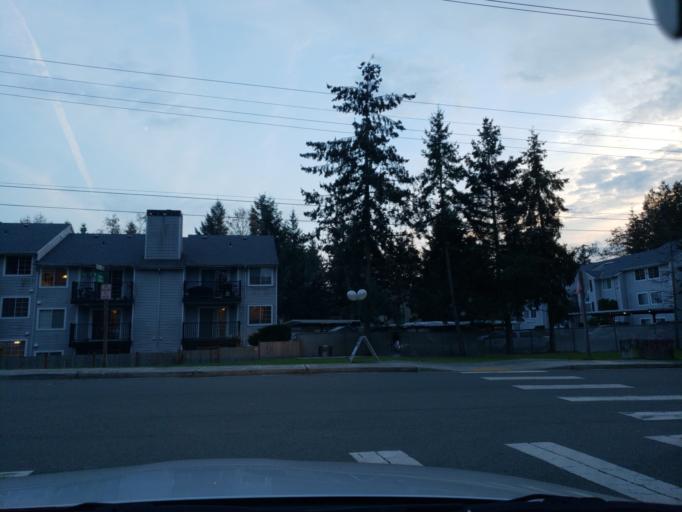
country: US
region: Washington
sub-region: King County
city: Kenmore
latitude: 47.7626
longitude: -122.2446
